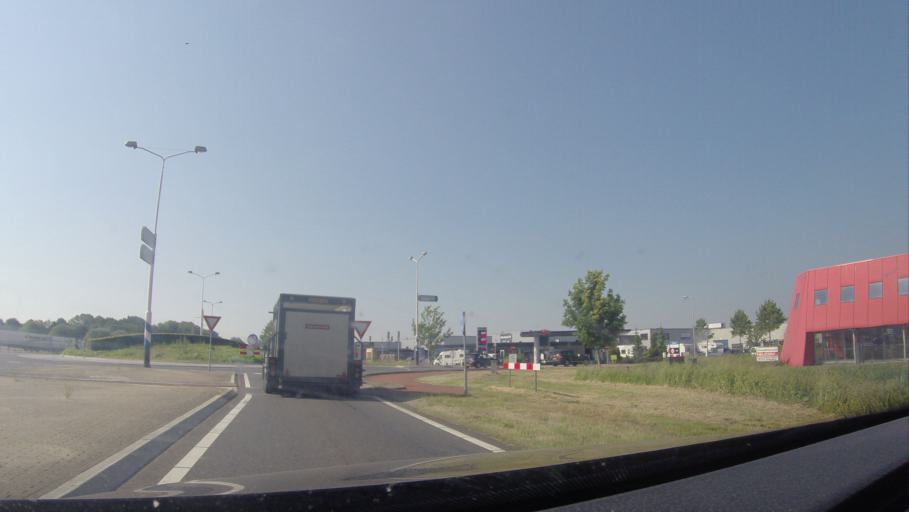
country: NL
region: Gelderland
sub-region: Gemeente Lochem
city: Laren
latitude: 52.2784
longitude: 6.4013
